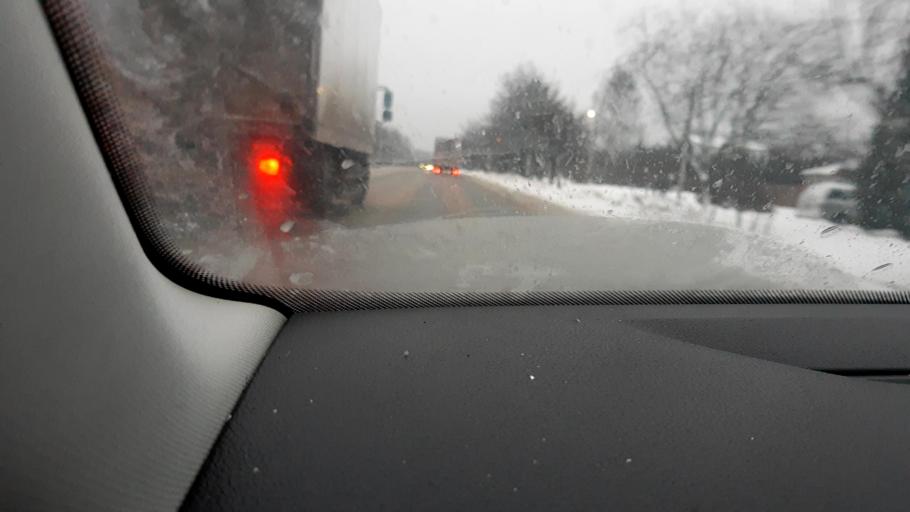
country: RU
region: Moskovskaya
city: Troitsk
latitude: 55.3047
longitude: 37.2197
